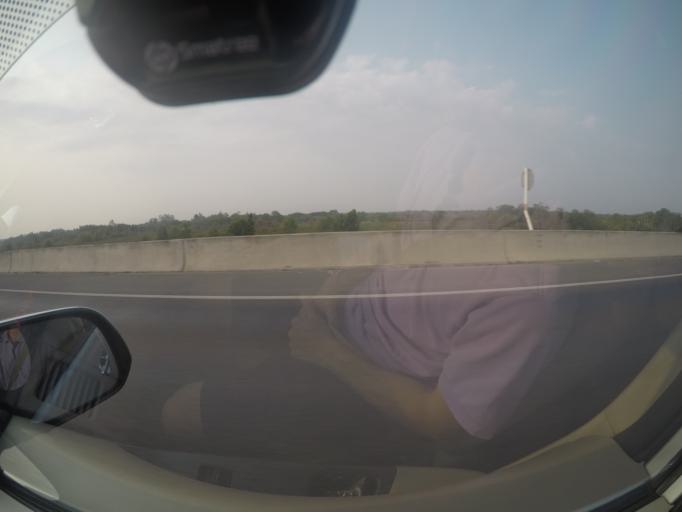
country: VN
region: Dong Nai
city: Nhon Trach
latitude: 10.7869
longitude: 106.8423
